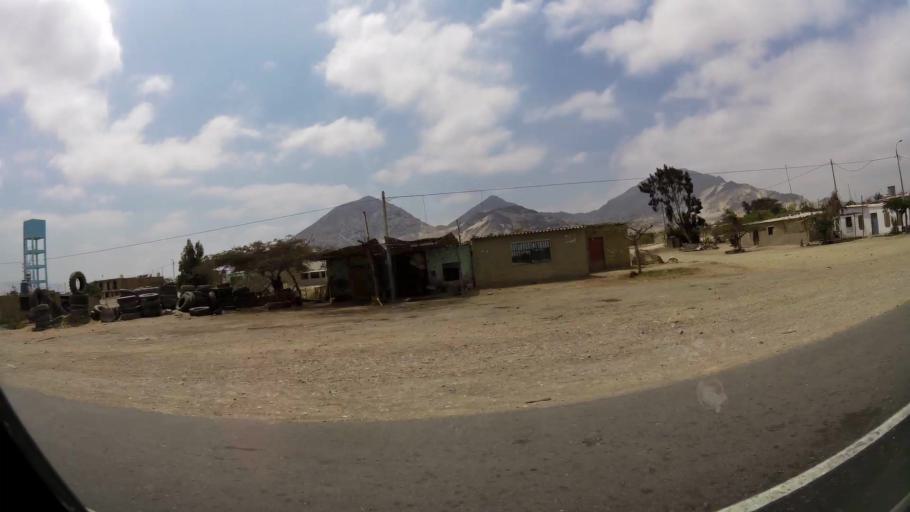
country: PE
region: La Libertad
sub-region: Ascope
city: Paijan
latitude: -7.6895
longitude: -79.3204
